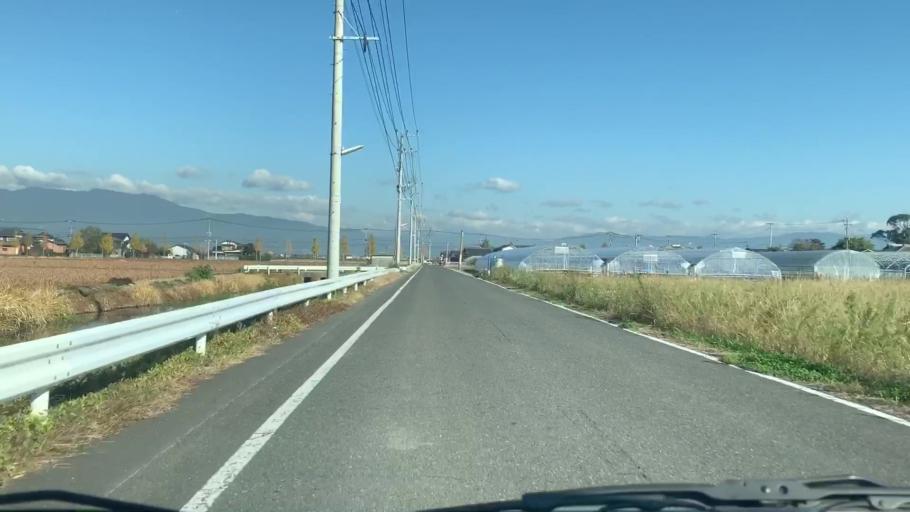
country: JP
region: Saga Prefecture
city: Saga-shi
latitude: 33.2523
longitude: 130.2579
